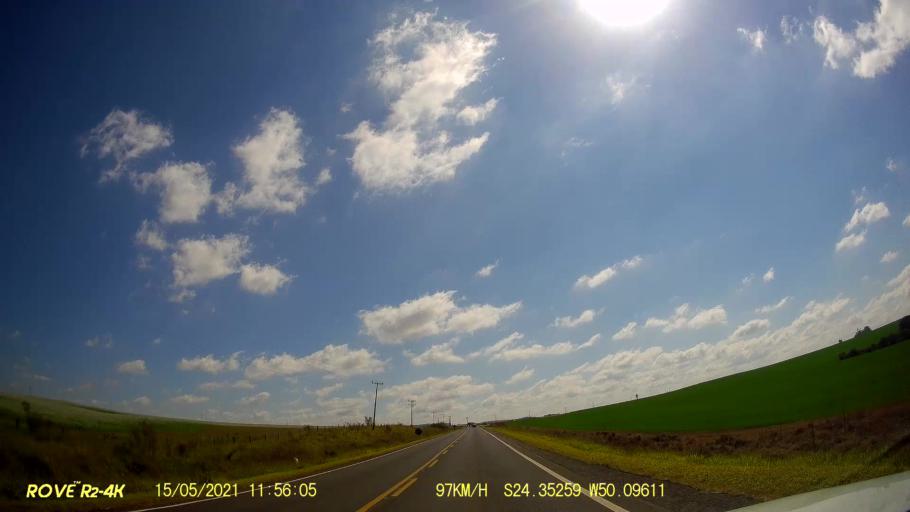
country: BR
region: Parana
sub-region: Pirai Do Sul
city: Pirai do Sul
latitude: -24.3531
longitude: -50.0966
